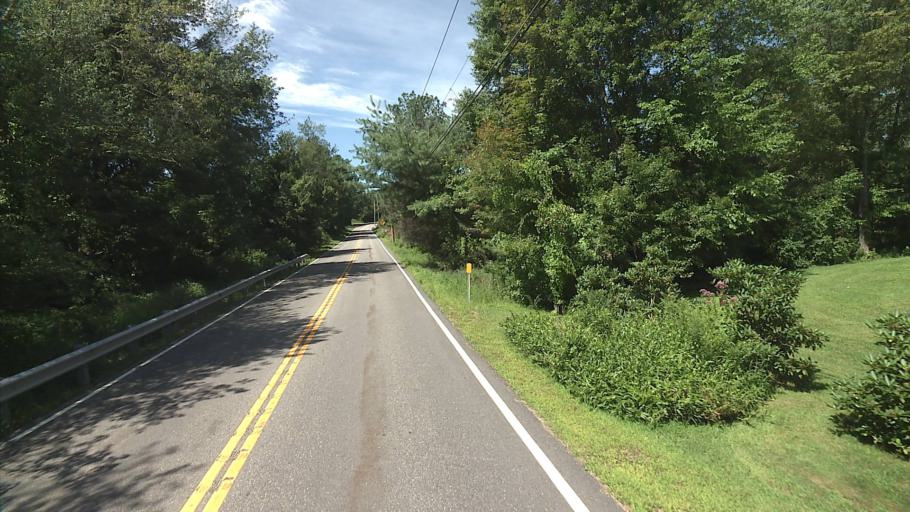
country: US
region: Connecticut
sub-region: Windham County
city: South Woodstock
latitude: 41.8952
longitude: -71.9884
